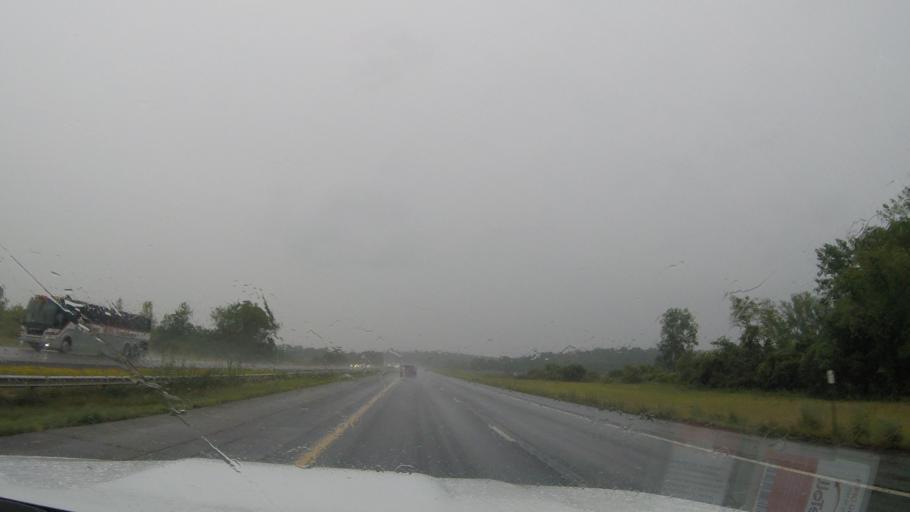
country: US
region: New York
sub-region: Seneca County
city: Bridgeport
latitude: 42.9988
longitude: -76.7266
